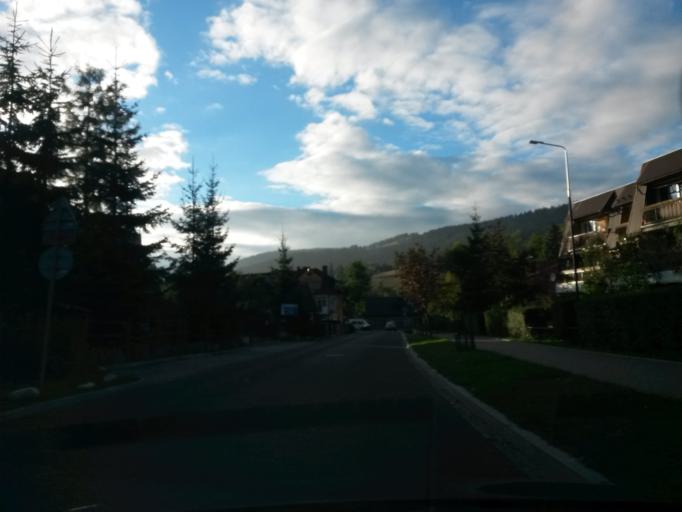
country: PL
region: Lesser Poland Voivodeship
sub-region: Powiat tatrzanski
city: Zakopane
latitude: 49.2931
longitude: 19.9443
